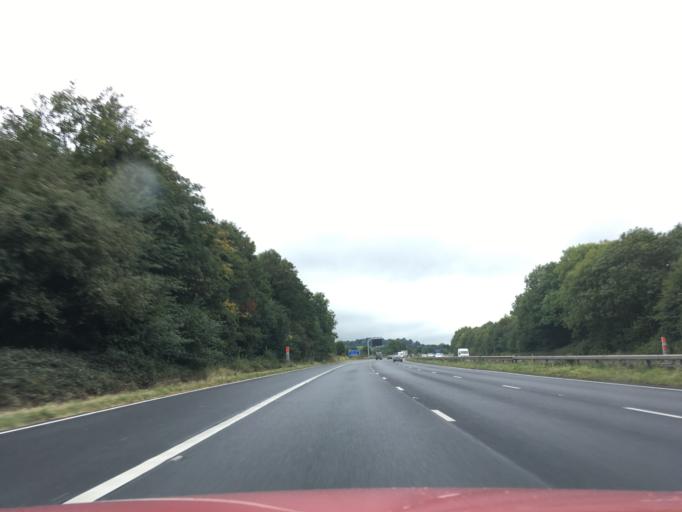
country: GB
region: England
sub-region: Gloucestershire
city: Barnwood
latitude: 51.8456
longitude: -2.1864
